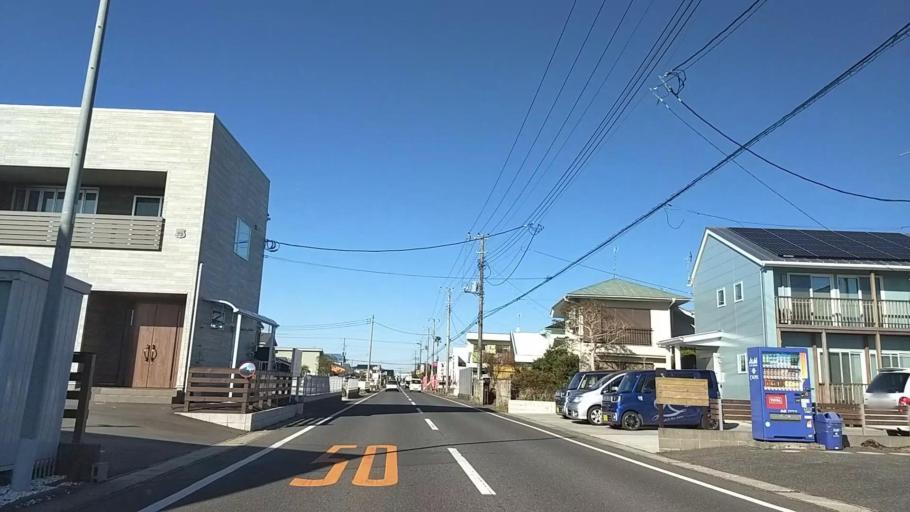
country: JP
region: Chiba
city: Ohara
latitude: 35.3532
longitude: 140.3893
